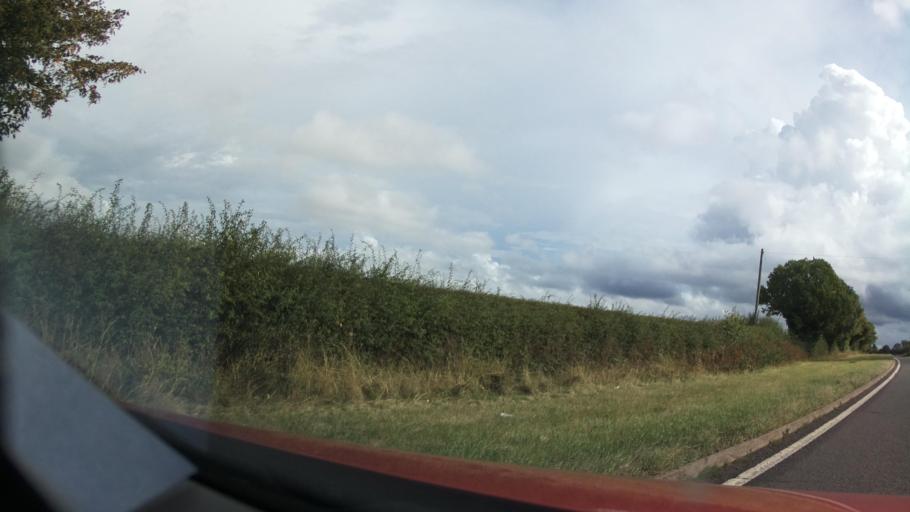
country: GB
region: England
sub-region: Shropshire
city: Ryton
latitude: 52.5892
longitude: -2.3983
